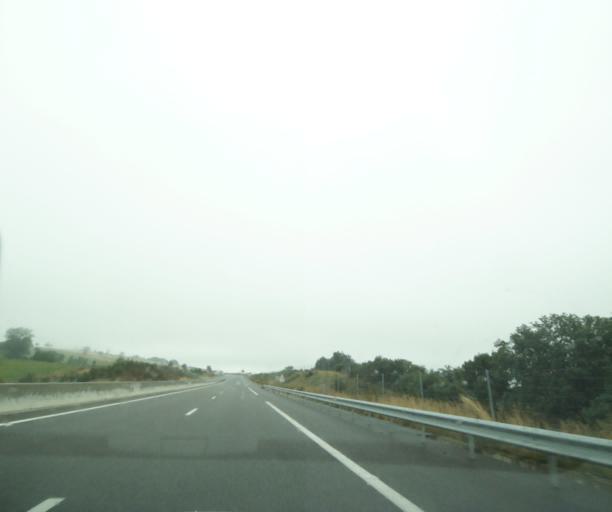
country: FR
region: Midi-Pyrenees
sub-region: Departement du Tarn
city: Carmaux
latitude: 44.0795
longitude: 2.2464
